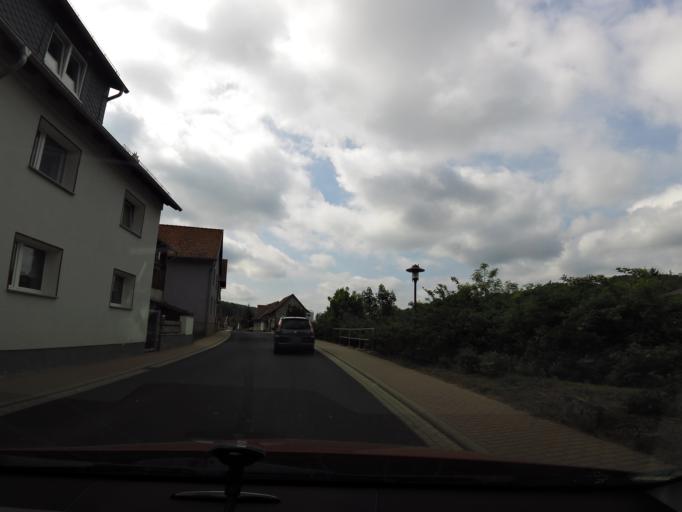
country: DE
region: Thuringia
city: Hallungen
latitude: 51.1184
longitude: 10.3361
